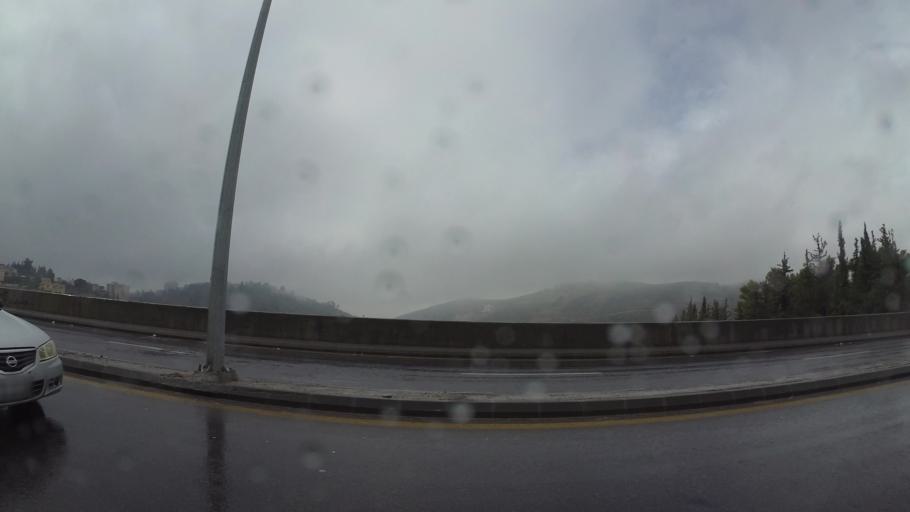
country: JO
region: Amman
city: Wadi as Sir
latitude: 32.0087
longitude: 35.7893
